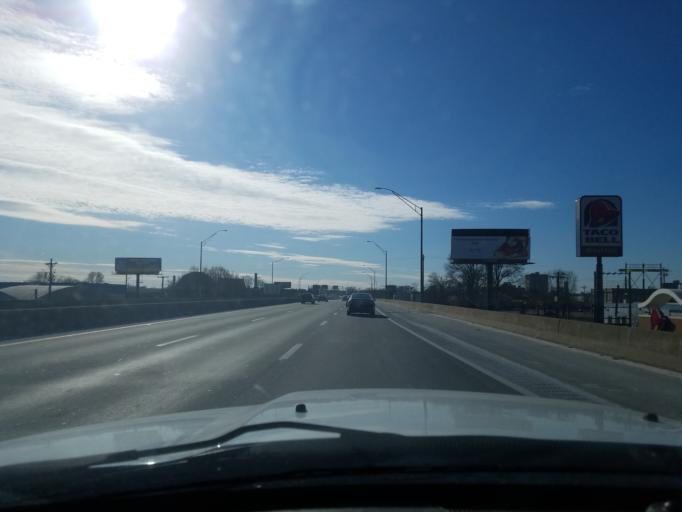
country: US
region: Kentucky
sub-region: Jefferson County
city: Louisville
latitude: 38.2456
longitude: -85.7524
